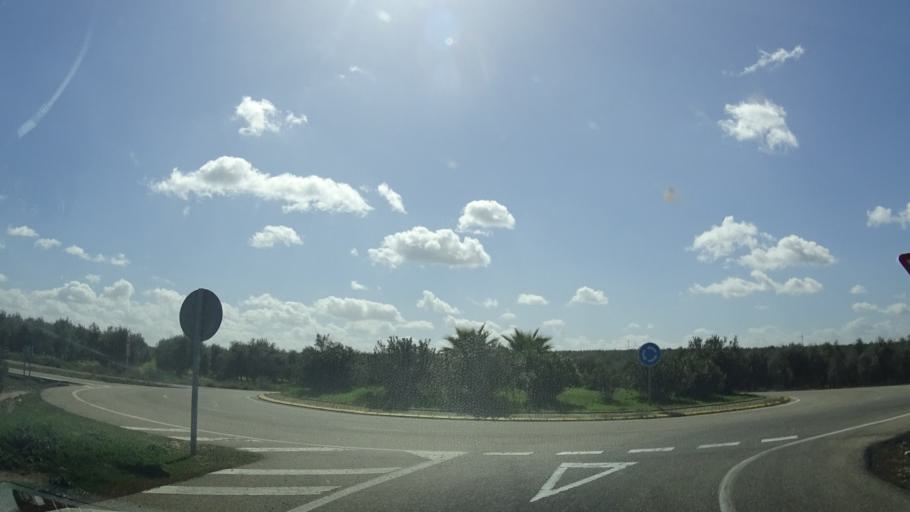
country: ES
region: Andalusia
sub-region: Province of Cordoba
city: Montoro
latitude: 38.0024
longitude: -4.3459
